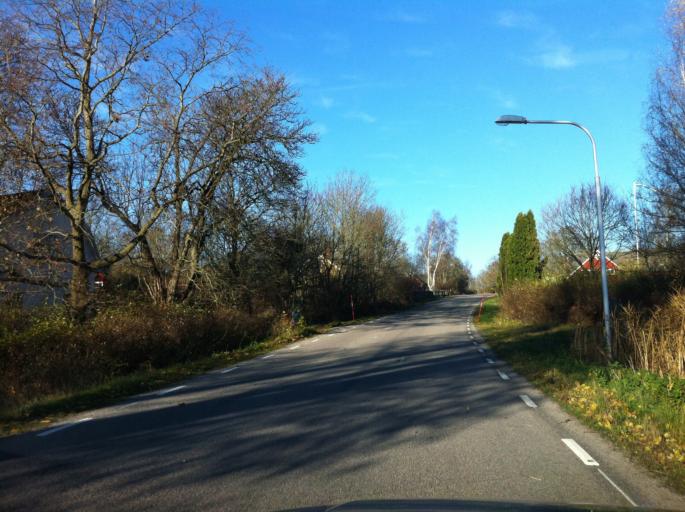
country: SE
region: Blekinge
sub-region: Ronneby Kommun
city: Brakne-Hoby
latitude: 56.1810
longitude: 15.1213
